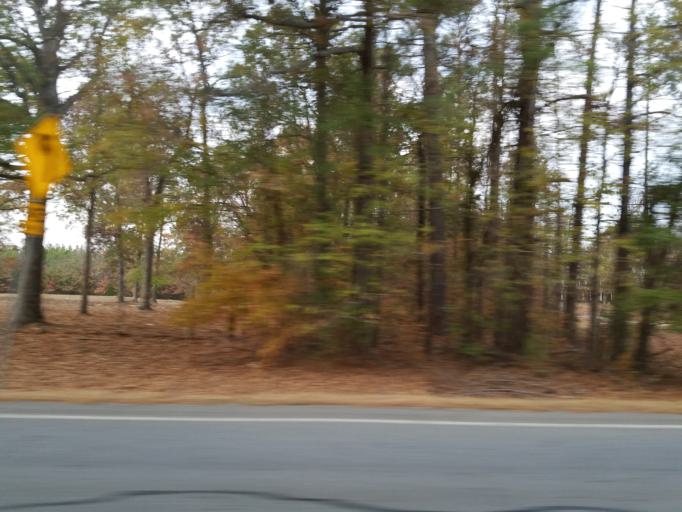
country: US
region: Georgia
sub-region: Gordon County
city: Calhoun
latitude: 34.6006
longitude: -84.8848
